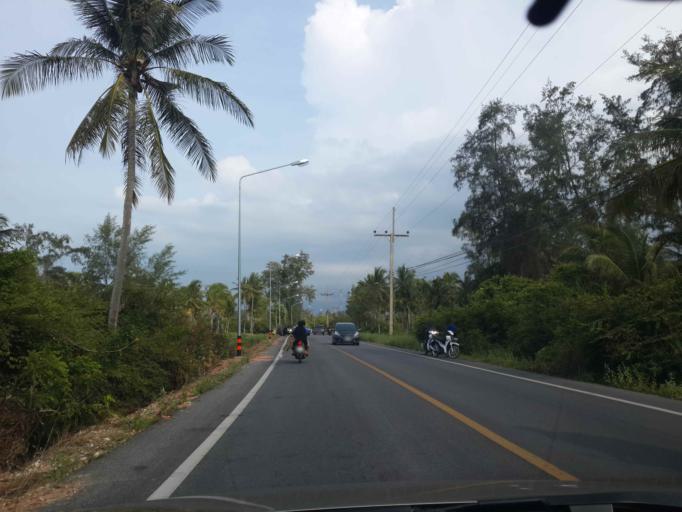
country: TH
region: Pattani
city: Yaring
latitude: 6.9004
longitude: 101.3614
